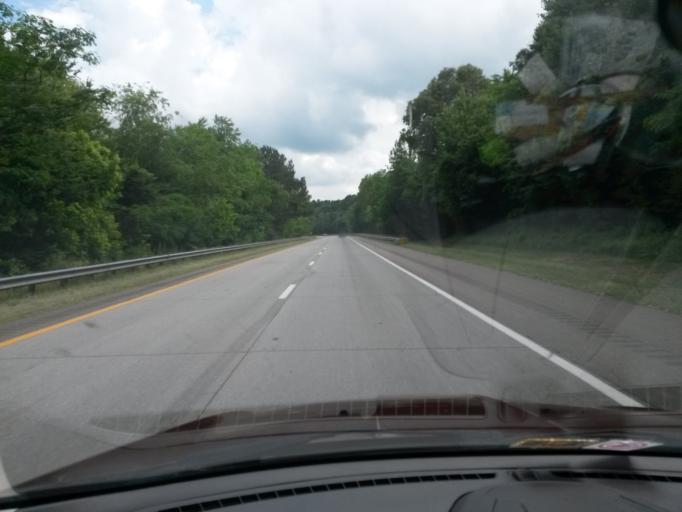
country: US
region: North Carolina
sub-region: Surry County
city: Elkin
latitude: 36.2672
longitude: -80.8257
